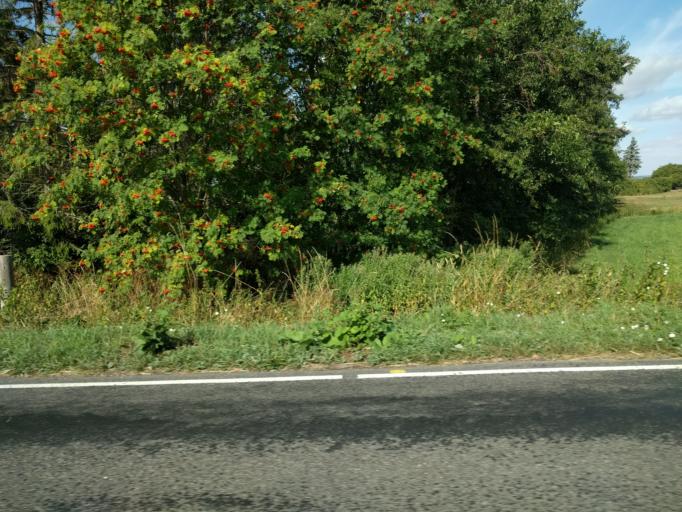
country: DK
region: Zealand
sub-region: Vordingborg Kommune
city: Stege
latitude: 54.9583
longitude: 12.2409
